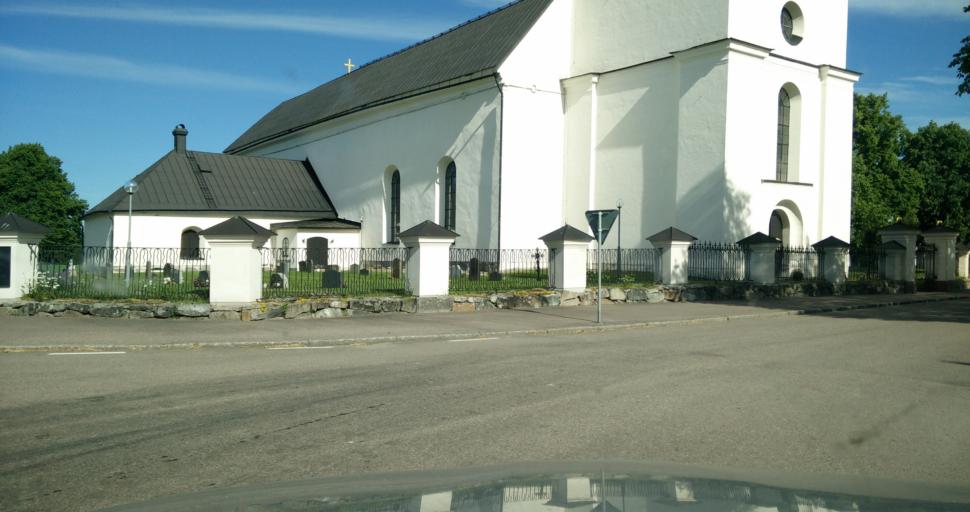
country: SE
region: Dalarna
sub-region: Hedemora Kommun
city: Langshyttan
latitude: 60.3887
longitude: 15.9995
